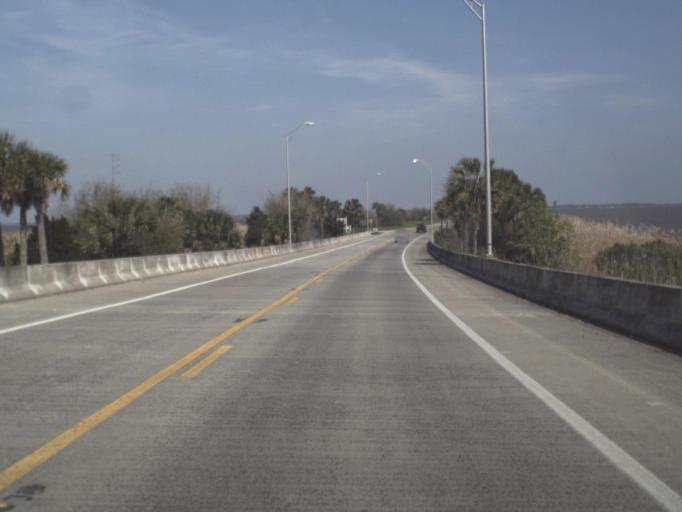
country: US
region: Florida
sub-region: Franklin County
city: Apalachicola
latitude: 29.7256
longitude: -84.9735
